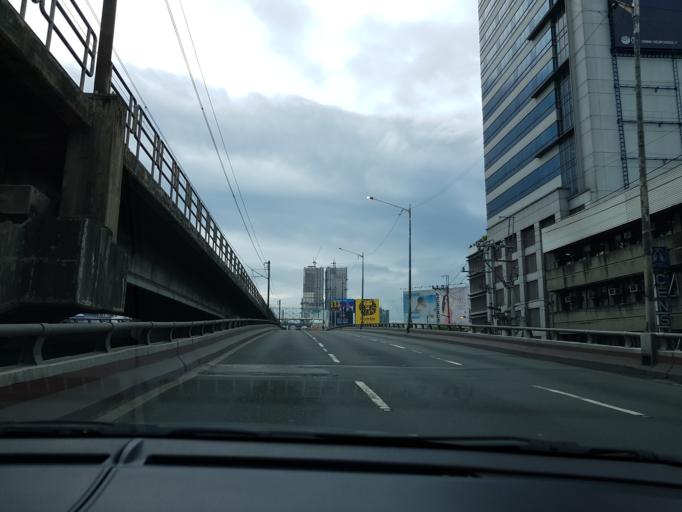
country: PH
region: Metro Manila
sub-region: Quezon City
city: Quezon City
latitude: 14.6454
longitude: 121.0367
